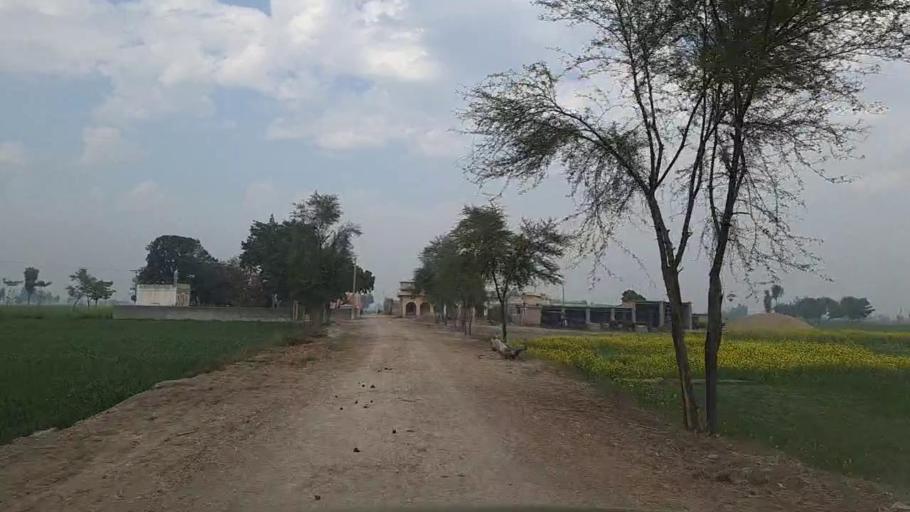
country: PK
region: Sindh
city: Nawabshah
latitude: 26.3564
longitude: 68.3921
